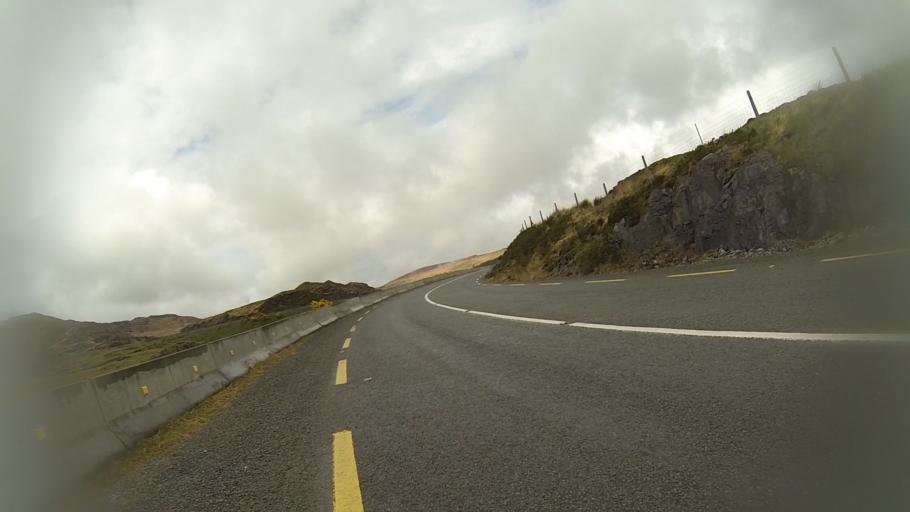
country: IE
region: Munster
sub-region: Ciarrai
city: Kenmare
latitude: 51.7960
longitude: -9.5834
